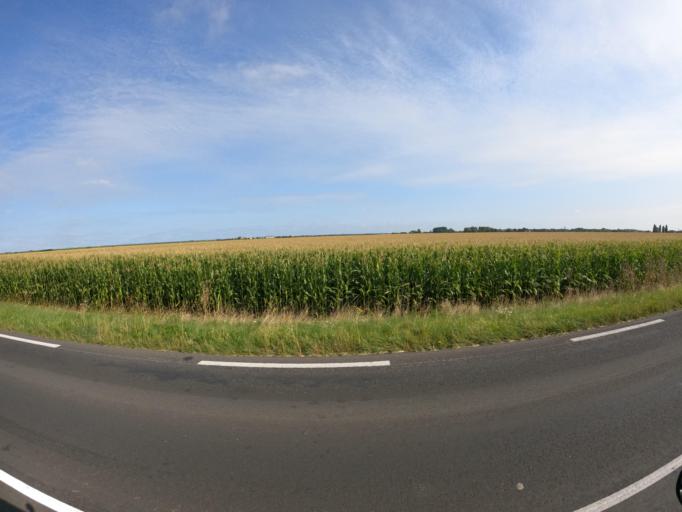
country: FR
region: Pays de la Loire
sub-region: Departement de la Vendee
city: Triaize
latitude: 46.3372
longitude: -1.2701
